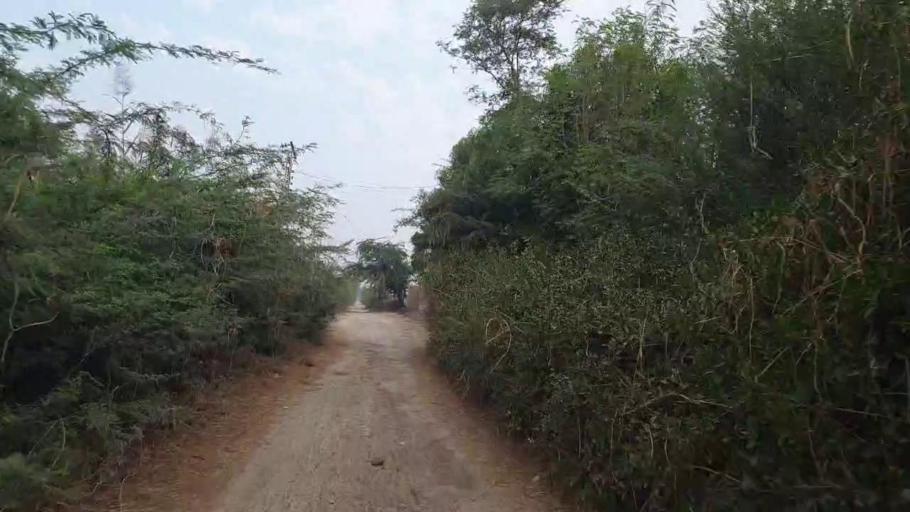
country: PK
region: Sindh
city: Talhar
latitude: 24.8345
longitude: 68.8804
